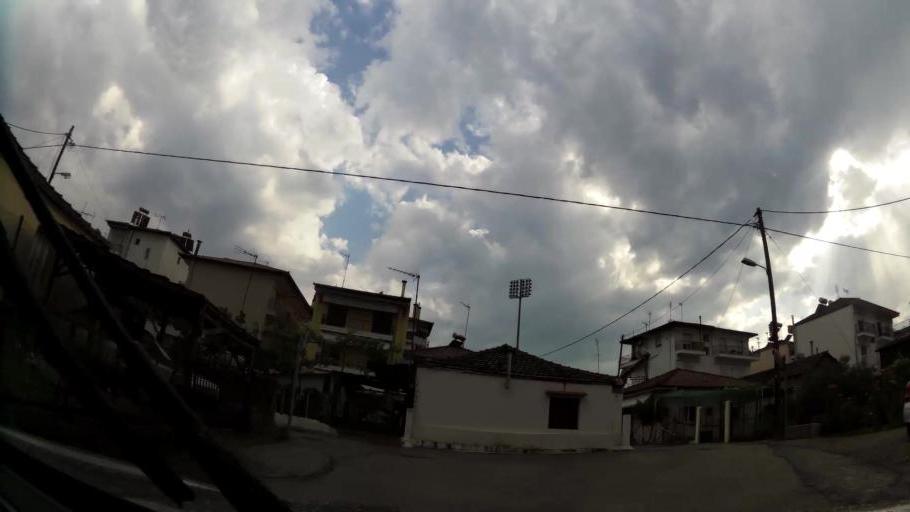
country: GR
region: Central Macedonia
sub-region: Nomos Imathias
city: Veroia
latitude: 40.5350
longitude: 22.2039
